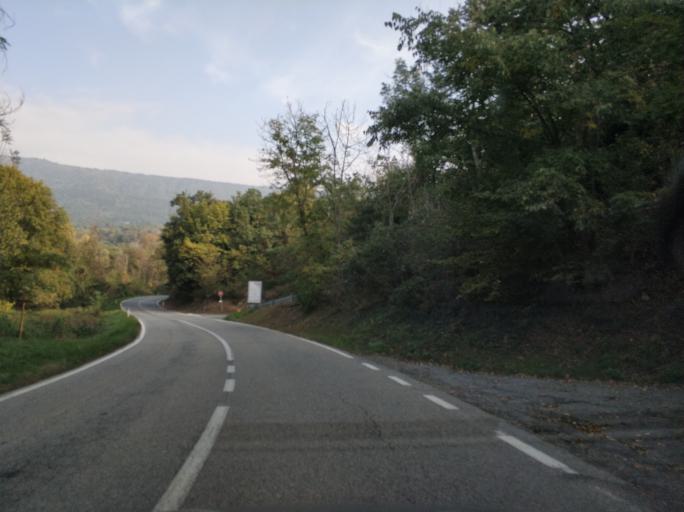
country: IT
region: Piedmont
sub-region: Provincia di Torino
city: Chiaverano
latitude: 45.4933
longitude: 7.8927
